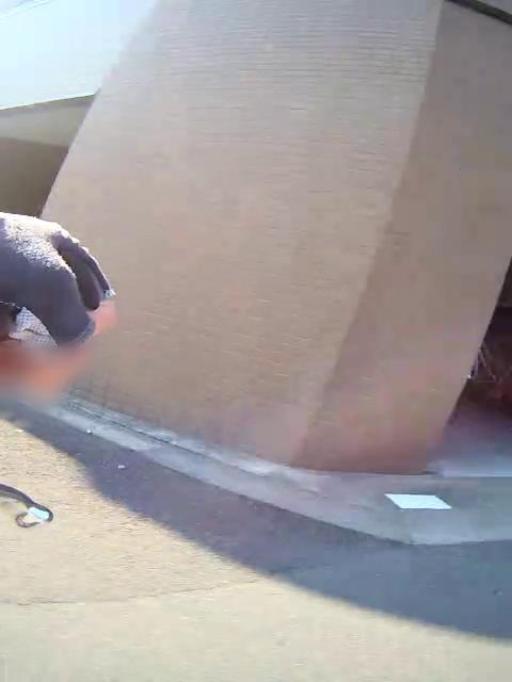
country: JP
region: Osaka
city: Suita
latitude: 34.7407
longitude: 135.5195
